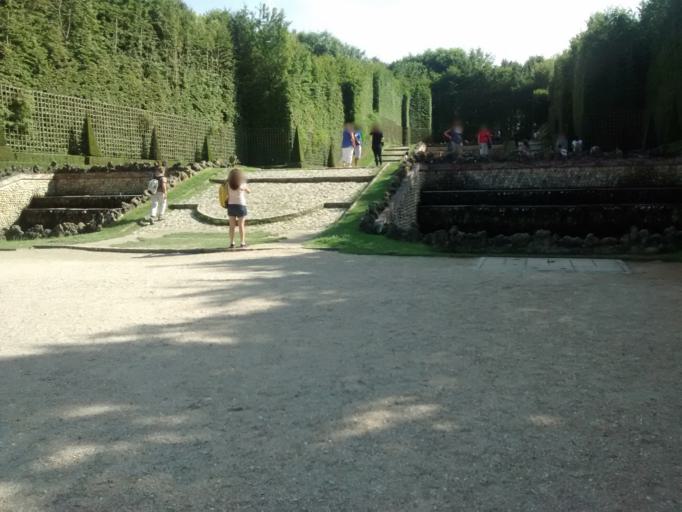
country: FR
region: Ile-de-France
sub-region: Departement des Yvelines
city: Le Chesnay
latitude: 48.8078
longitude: 2.1208
